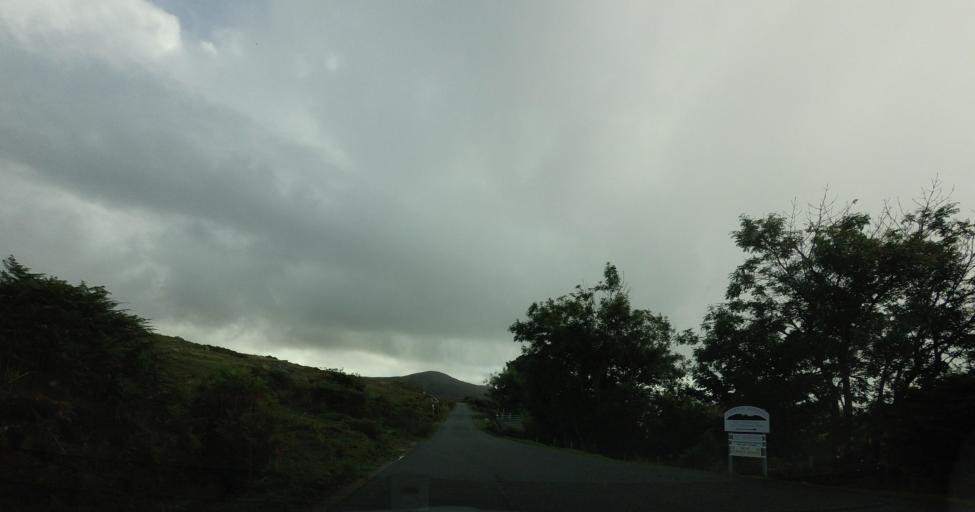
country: GB
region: Scotland
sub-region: Highland
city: Portree
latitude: 57.2112
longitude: -6.0077
